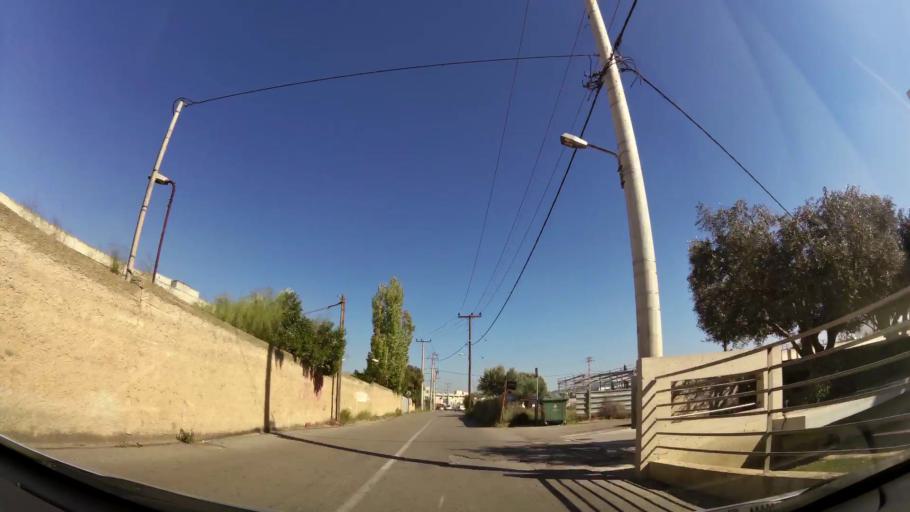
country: GR
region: Attica
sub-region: Nomarchia Athinas
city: Lykovrysi
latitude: 38.0745
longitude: 23.7773
